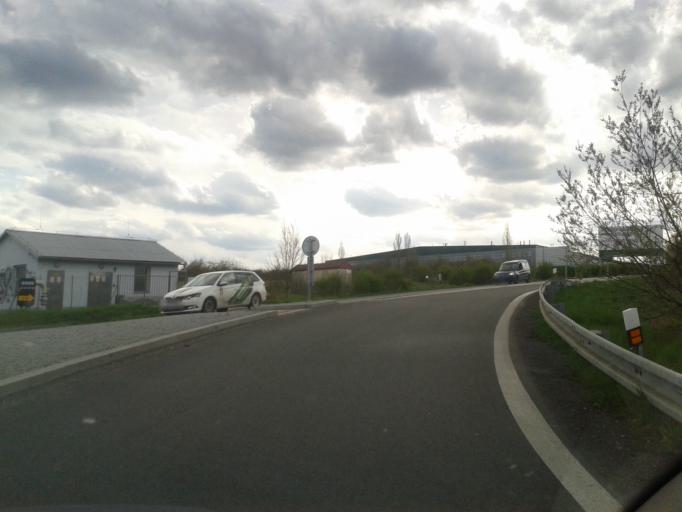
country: CZ
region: Central Bohemia
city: Rudna
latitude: 50.0236
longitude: 14.2060
